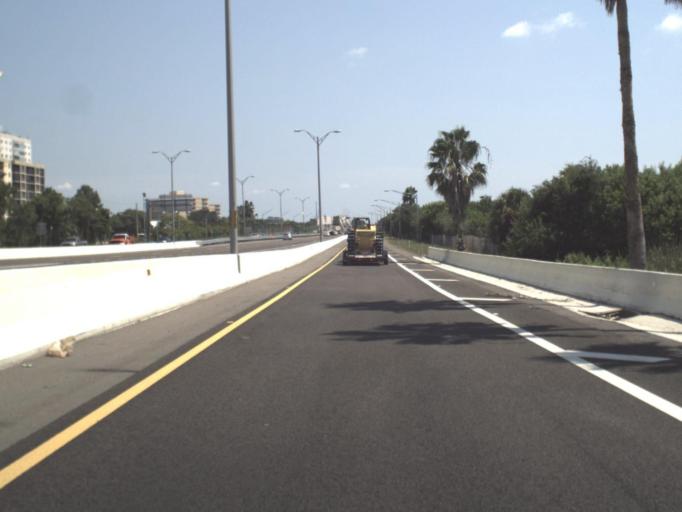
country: US
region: Florida
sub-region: Pinellas County
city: Tierra Verde
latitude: 27.7063
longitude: -82.6795
